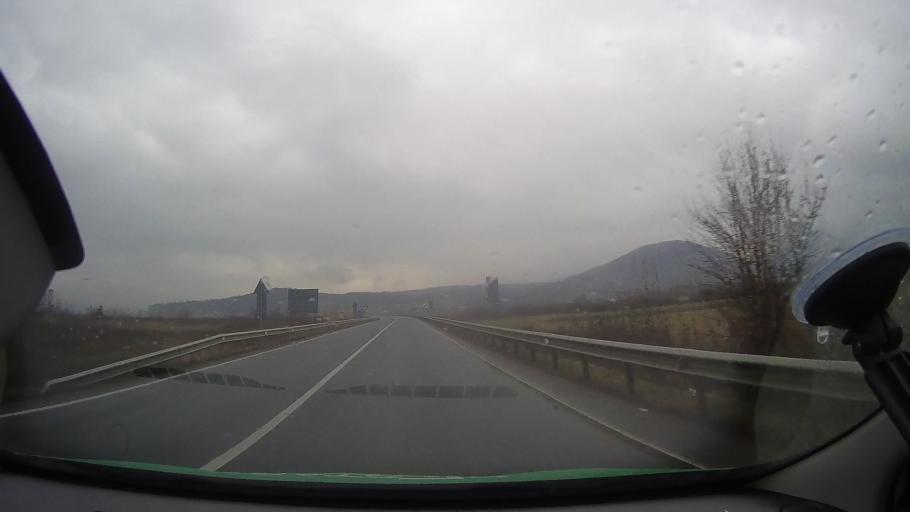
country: RO
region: Hunedoara
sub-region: Comuna Baia de Cris
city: Baia de Cris
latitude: 46.1801
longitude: 22.6821
